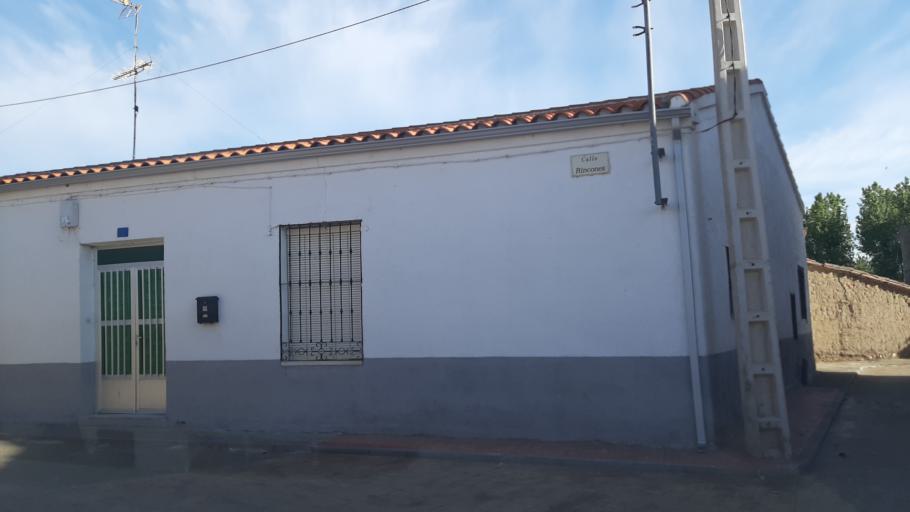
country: ES
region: Castille and Leon
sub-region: Provincia de Salamanca
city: Gajates
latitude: 40.7834
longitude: -5.3658
